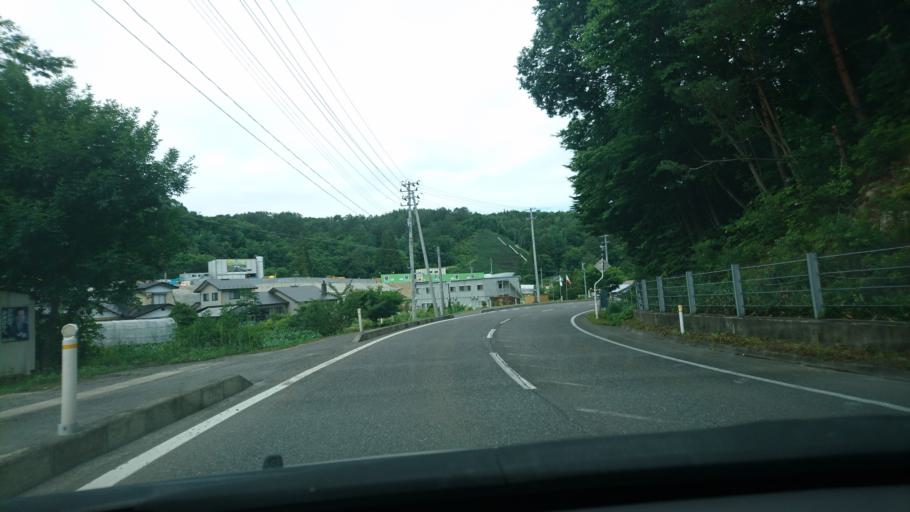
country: JP
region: Iwate
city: Miyako
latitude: 39.9589
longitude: 141.8450
